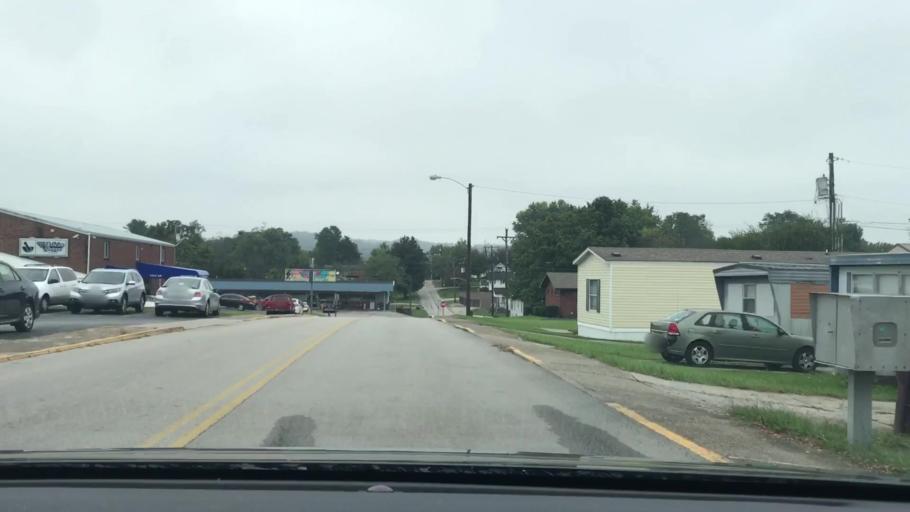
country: US
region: Kentucky
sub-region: Pulaski County
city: Somerset
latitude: 37.0969
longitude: -84.5926
